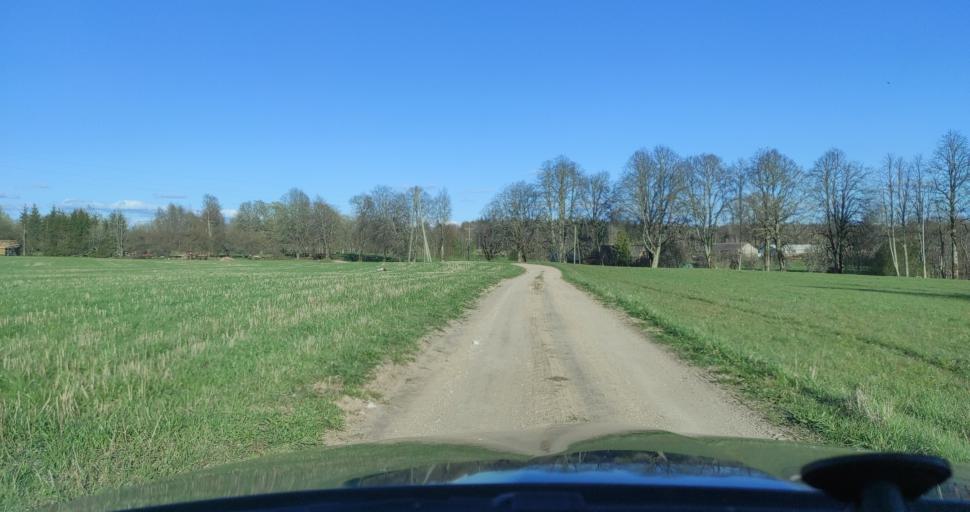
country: LV
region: Kuldigas Rajons
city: Kuldiga
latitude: 56.8693
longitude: 21.8427
